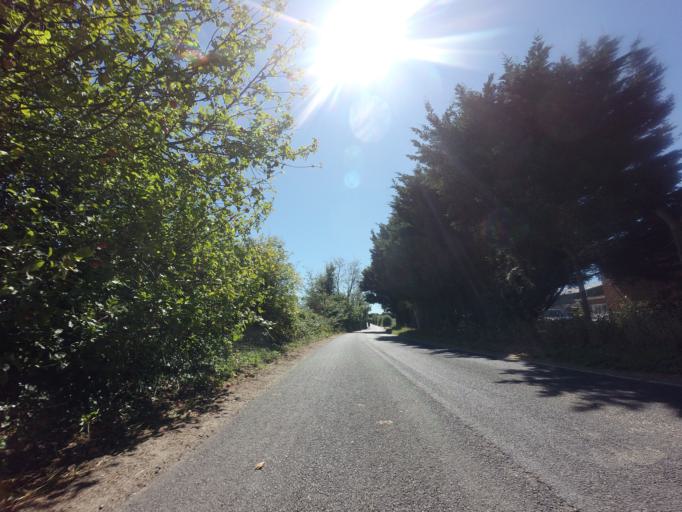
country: GB
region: England
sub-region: Kent
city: Ash
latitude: 51.2715
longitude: 1.2964
